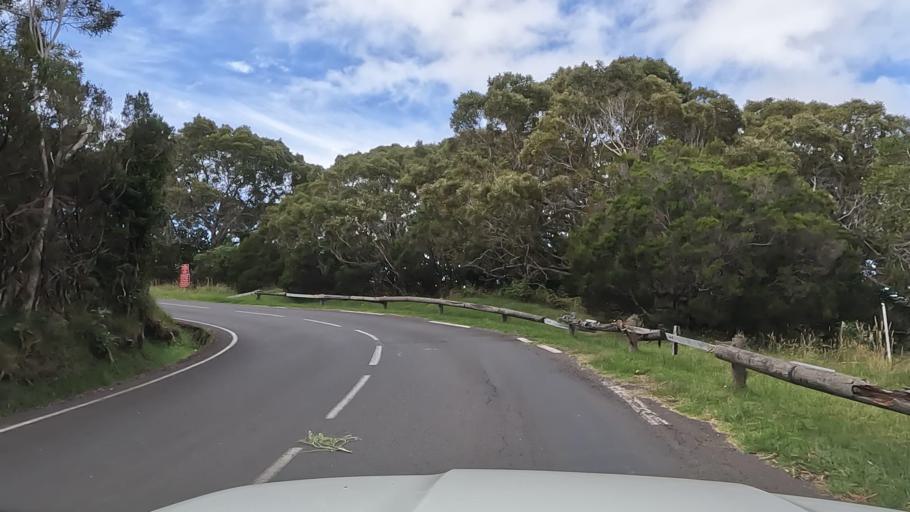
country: RE
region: Reunion
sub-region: Reunion
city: Le Tampon
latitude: -21.2416
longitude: 55.5859
